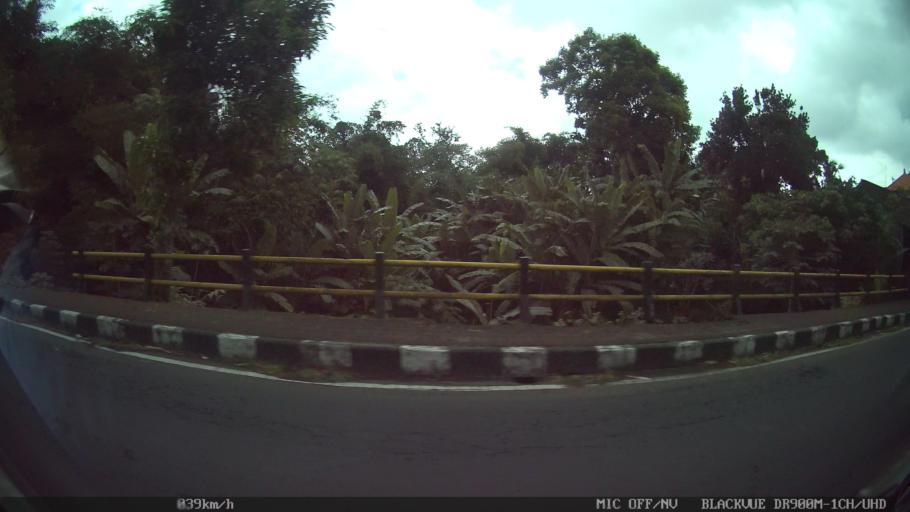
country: ID
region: Bali
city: Banjar Mambalkajanan
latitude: -8.5510
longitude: 115.2286
